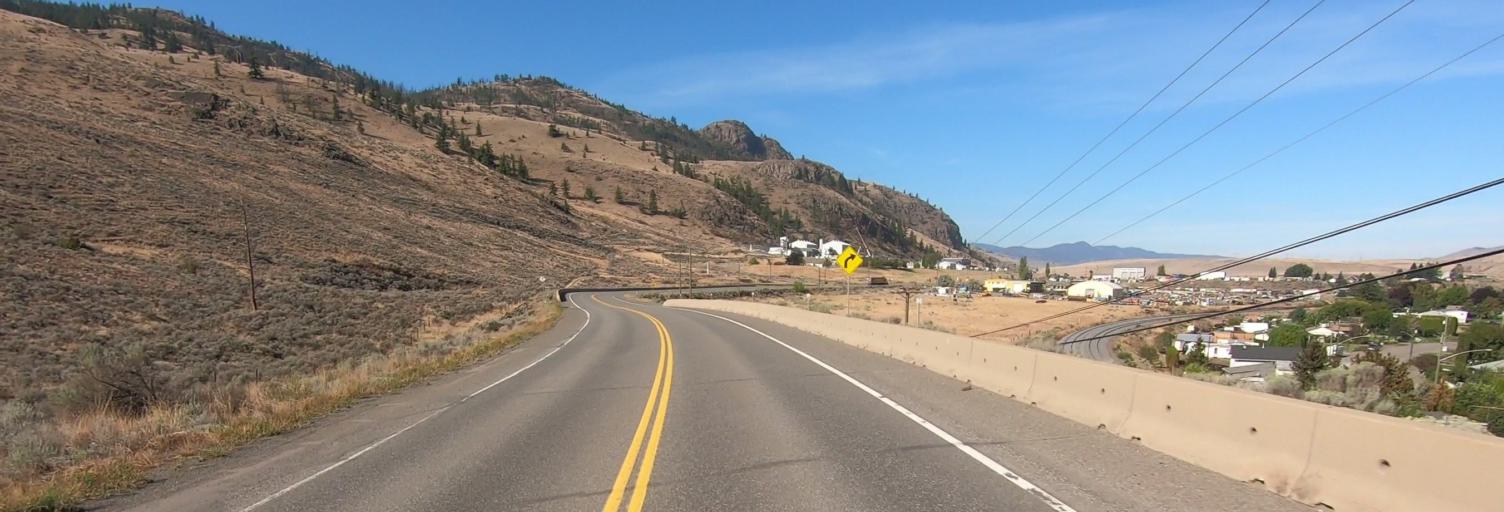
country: CA
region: British Columbia
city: Logan Lake
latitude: 50.7513
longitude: -120.8455
